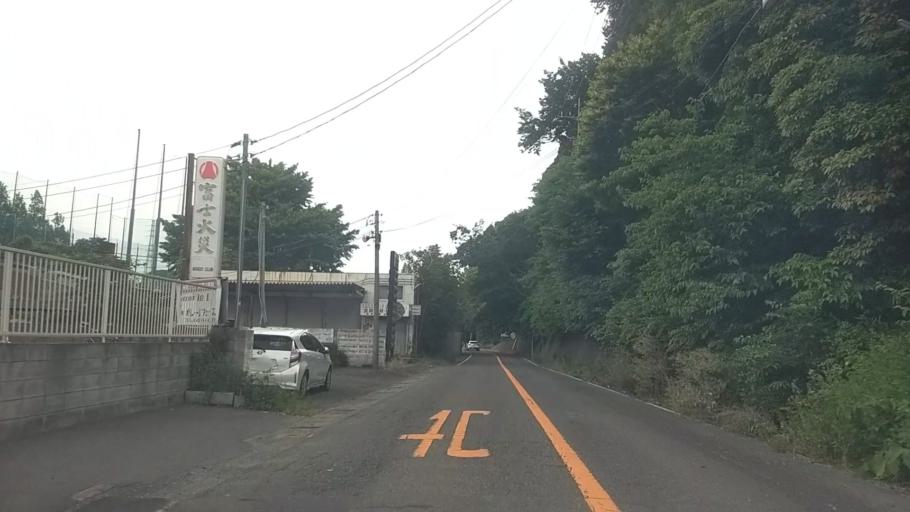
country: JP
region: Kanagawa
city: Fujisawa
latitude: 35.3575
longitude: 139.4353
